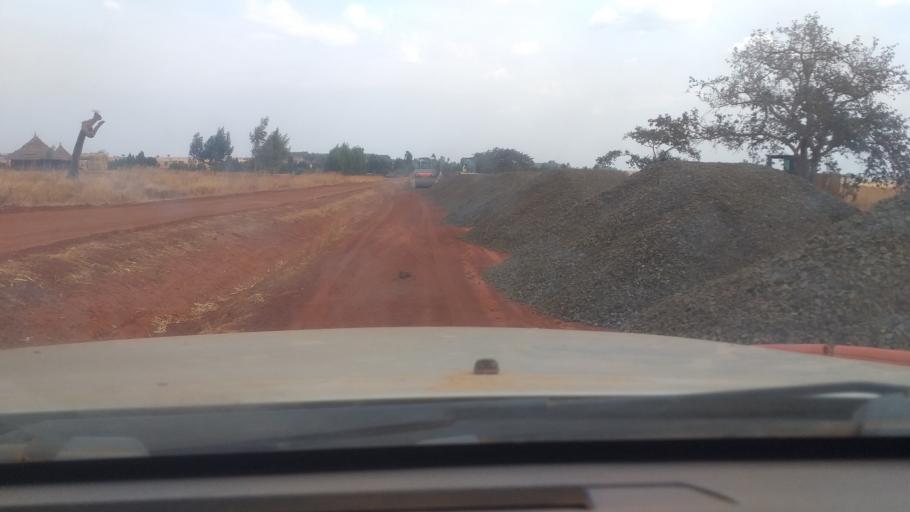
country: ET
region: Binshangul Gumuz
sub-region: Asosa
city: Asosa
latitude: 10.0802
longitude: 34.6207
